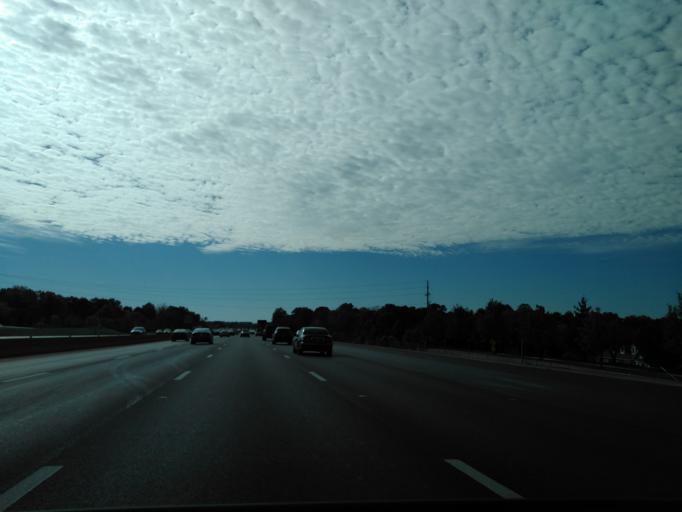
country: US
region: Missouri
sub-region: Saint Louis County
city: Creve Coeur
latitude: 38.6612
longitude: -90.4486
